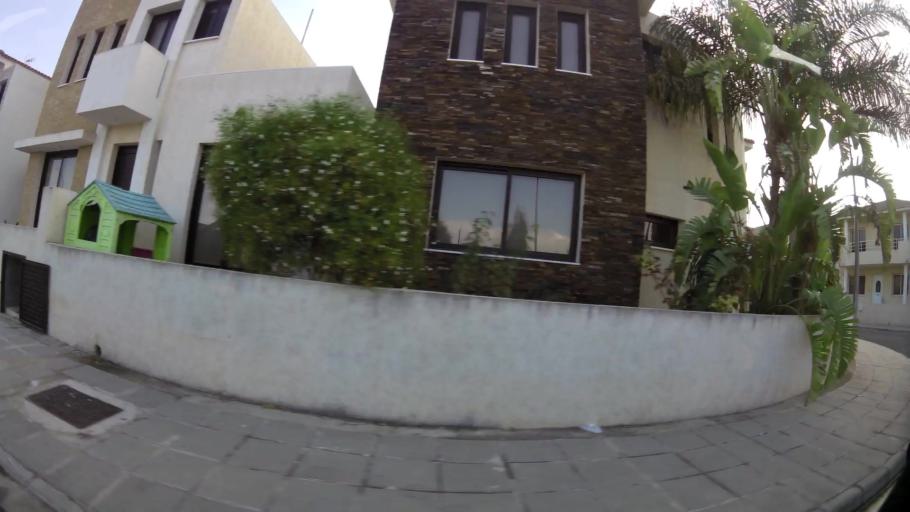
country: CY
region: Larnaka
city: Livadia
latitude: 34.9423
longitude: 33.6120
